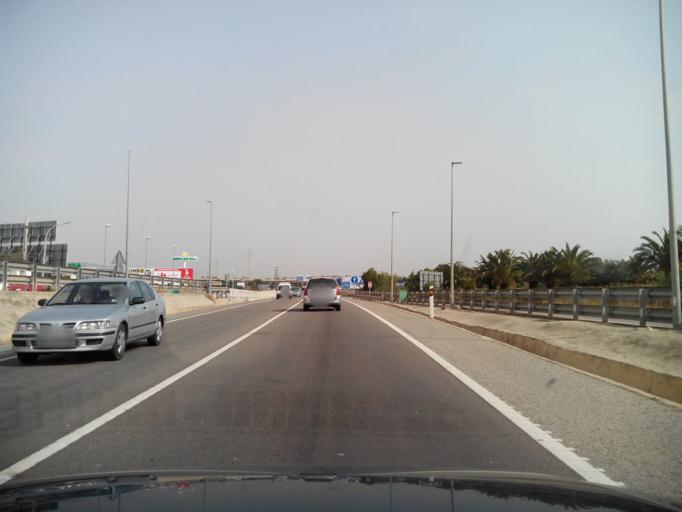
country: ES
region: Catalonia
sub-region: Provincia de Tarragona
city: El Vendrell
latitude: 41.1906
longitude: 1.5216
